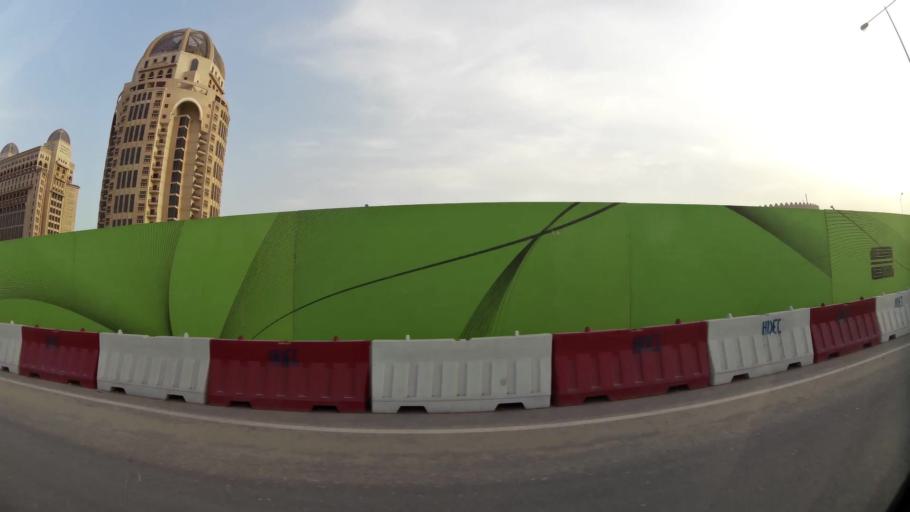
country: QA
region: Baladiyat ad Dawhah
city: Doha
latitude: 25.3515
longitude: 51.5260
